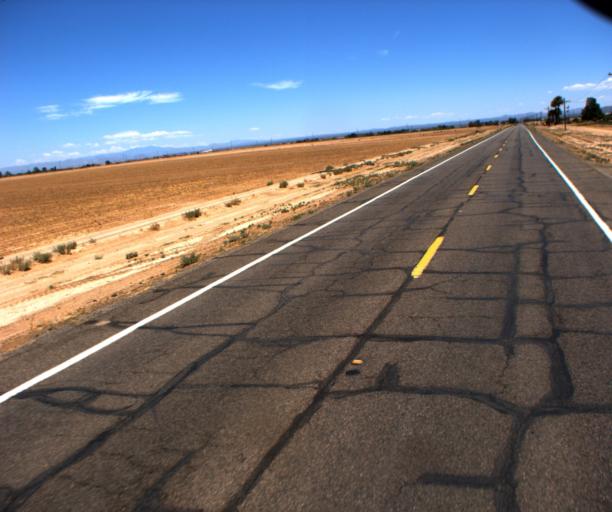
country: US
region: Arizona
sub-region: Pinal County
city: Coolidge
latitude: 32.8794
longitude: -111.5442
